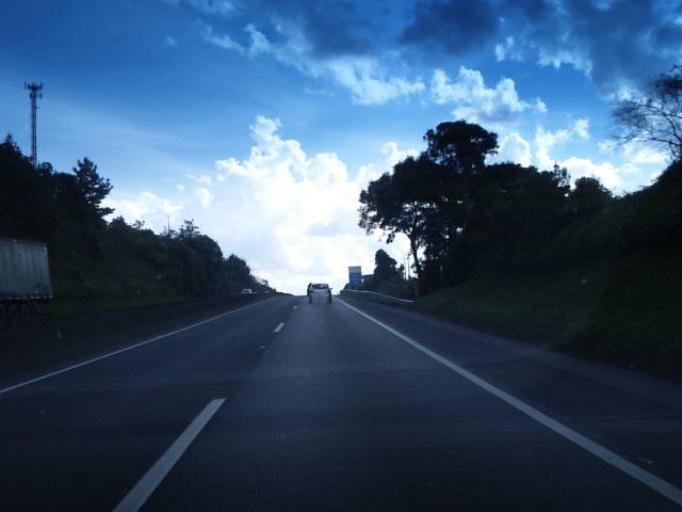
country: BR
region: Parana
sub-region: Campina Grande Do Sul
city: Campina Grande do Sul
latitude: -25.3357
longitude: -49.0354
